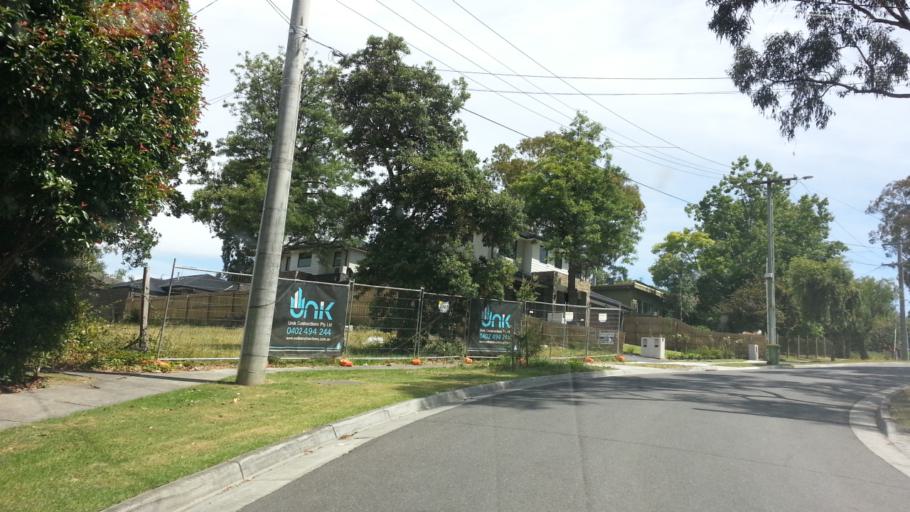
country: AU
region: Victoria
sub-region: Knox
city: Boronia
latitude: -37.8674
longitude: 145.2760
